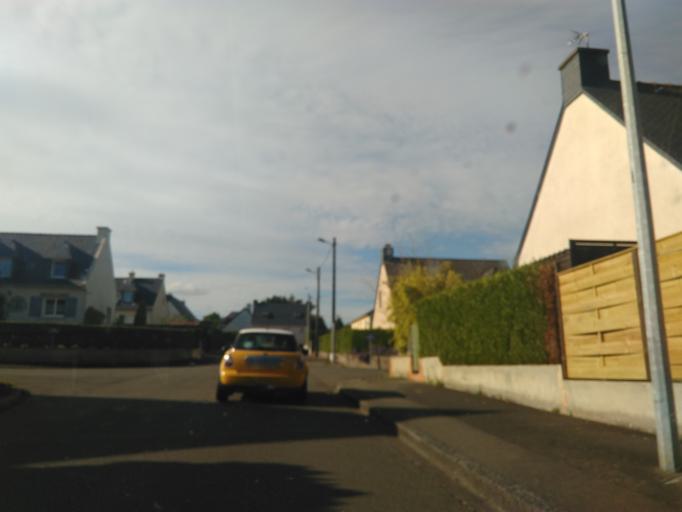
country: FR
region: Brittany
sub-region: Departement d'Ille-et-Vilaine
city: Pleumeleuc
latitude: 48.1844
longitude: -1.9220
